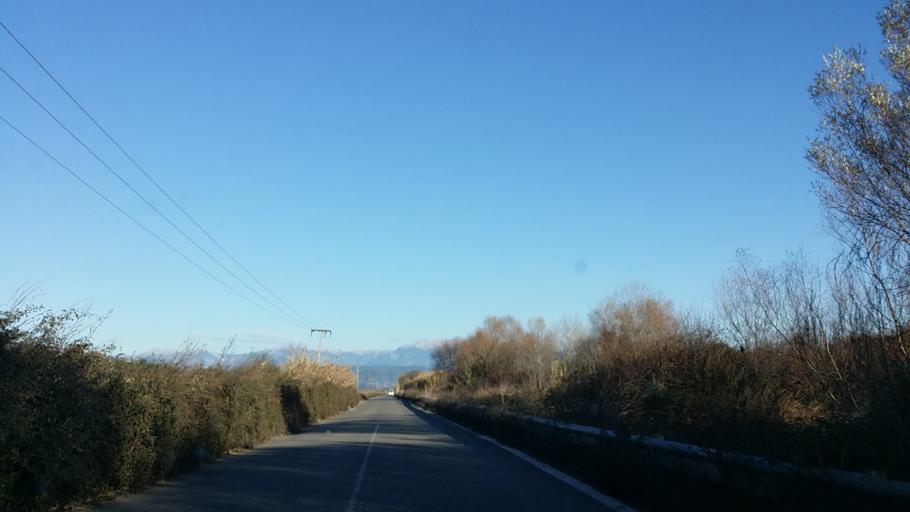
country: GR
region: West Greece
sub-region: Nomos Aitolias kai Akarnanias
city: Lepenou
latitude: 38.6437
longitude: 21.2634
